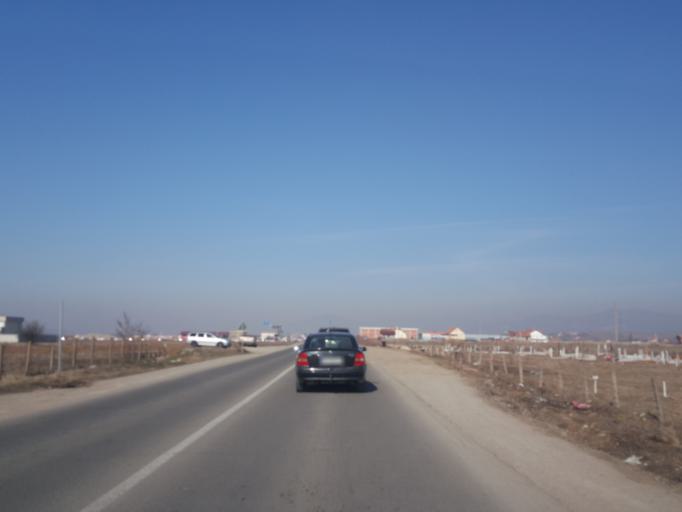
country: XK
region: Mitrovica
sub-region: Vushtrri
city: Vushtrri
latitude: 42.7873
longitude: 21.0076
